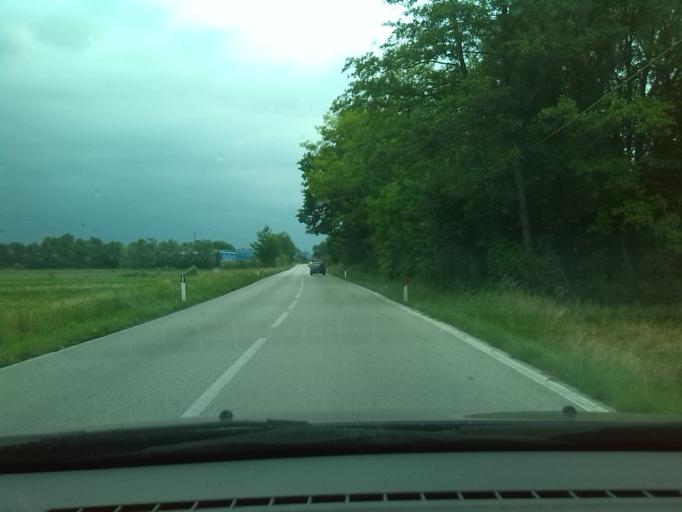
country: IT
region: Friuli Venezia Giulia
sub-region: Provincia di Udine
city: Treppo Grande
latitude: 46.2177
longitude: 13.1671
